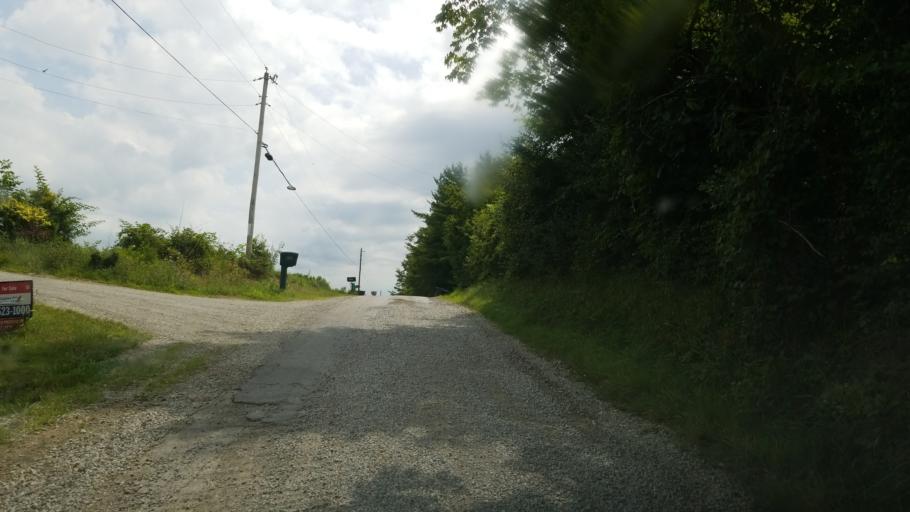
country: US
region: Ohio
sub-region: Delaware County
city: Sunbury
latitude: 40.3256
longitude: -82.8087
